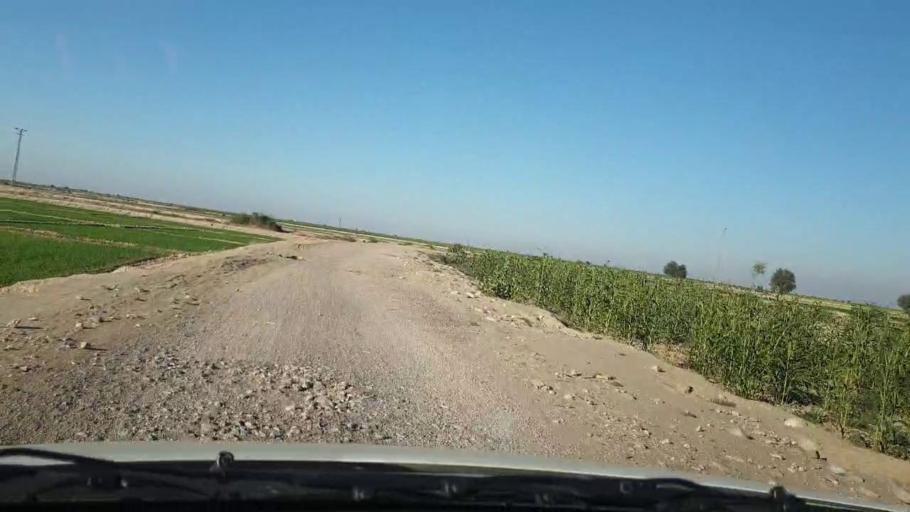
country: PK
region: Sindh
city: Johi
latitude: 26.7403
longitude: 67.5033
